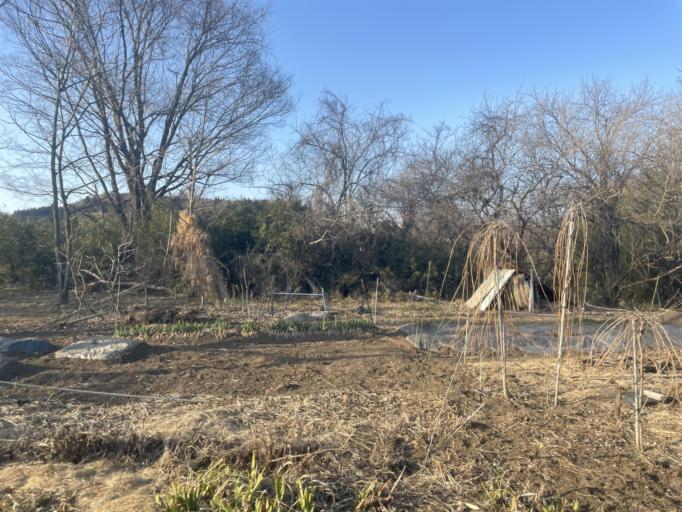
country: JP
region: Gunma
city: Nakanojomachi
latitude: 36.5855
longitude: 138.8595
